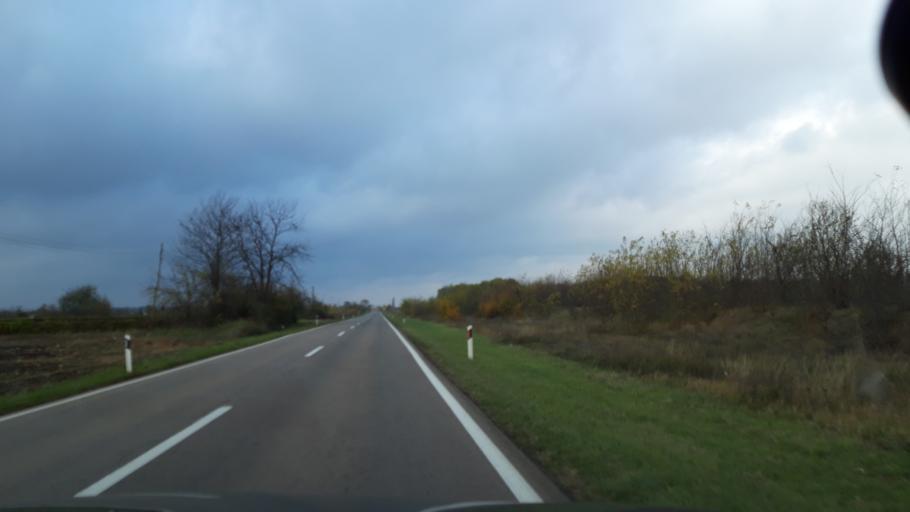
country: RS
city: Sanad
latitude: 45.9714
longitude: 20.1221
